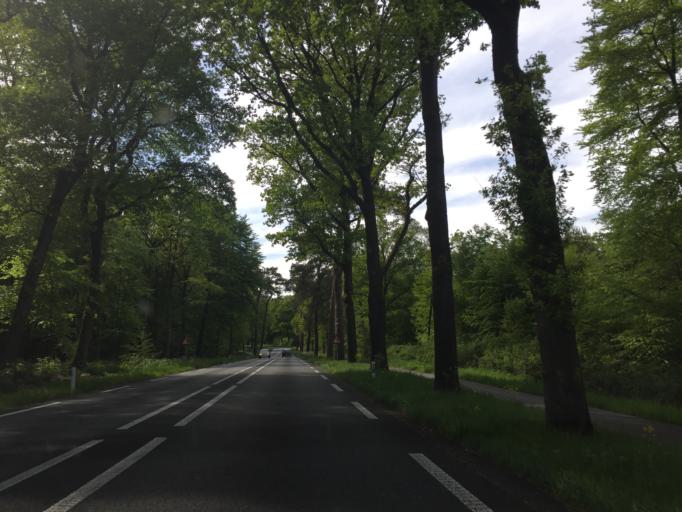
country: NL
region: Gelderland
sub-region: Gemeente Apeldoorn
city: Apeldoorn
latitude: 52.2316
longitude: 5.8936
